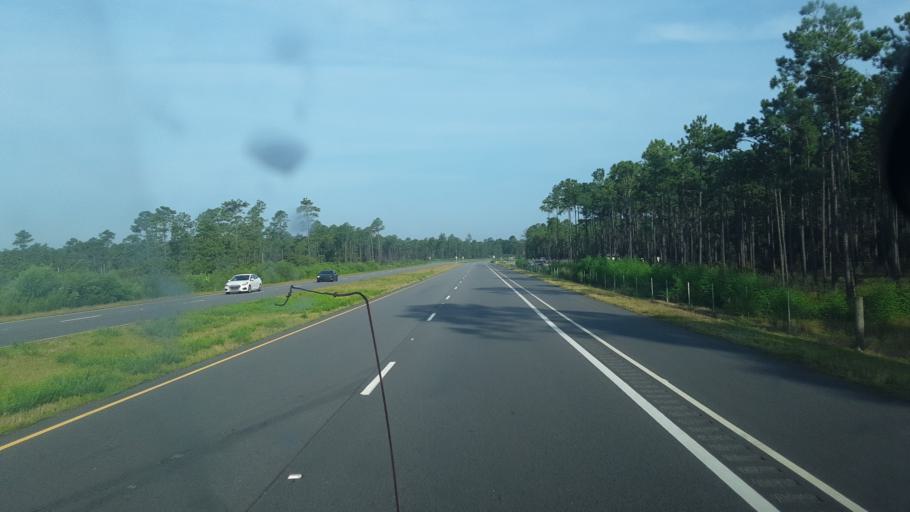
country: US
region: South Carolina
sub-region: Horry County
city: Forestbrook
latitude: 33.8046
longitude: -78.8892
